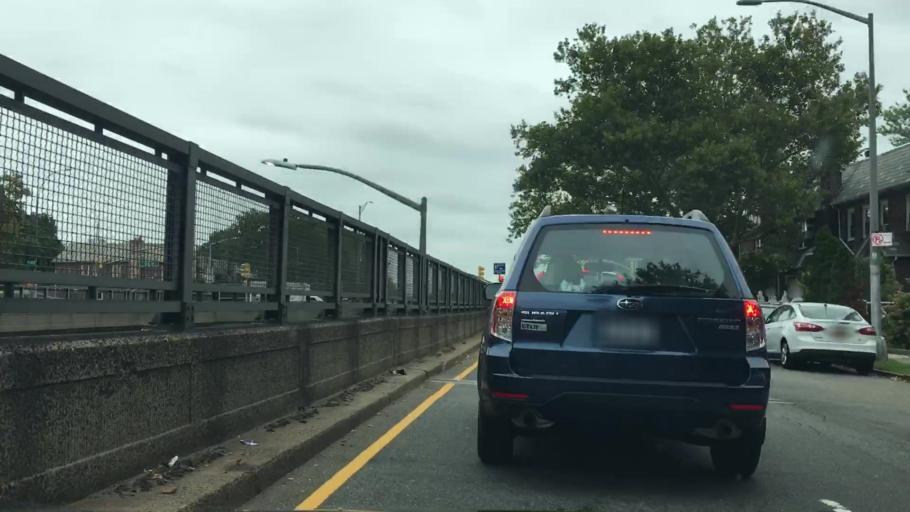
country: US
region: New York
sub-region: Queens County
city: Jamaica
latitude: 40.7160
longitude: -73.8040
